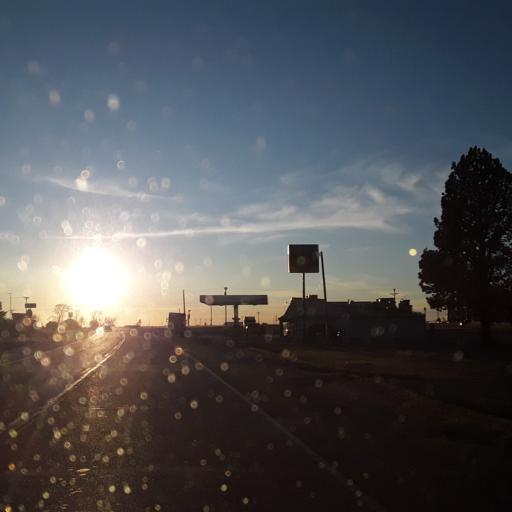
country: US
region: Colorado
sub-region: Cheyenne County
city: Cheyenne Wells
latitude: 38.8198
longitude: -102.3408
